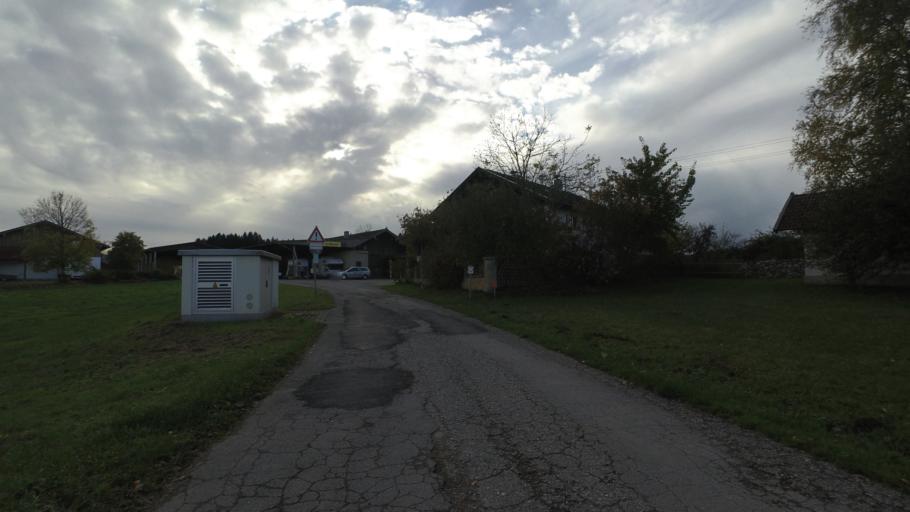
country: DE
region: Bavaria
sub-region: Upper Bavaria
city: Traunreut
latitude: 47.9349
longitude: 12.5929
